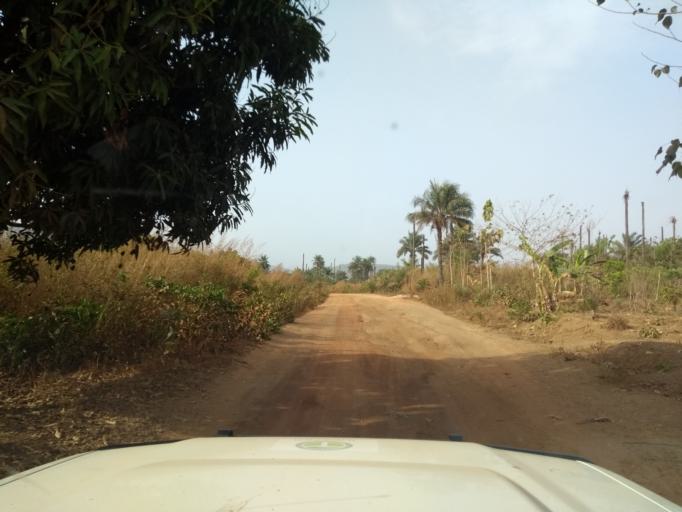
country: GN
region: Kindia
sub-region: Prefecture de Dubreka
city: Dubreka
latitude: 9.8802
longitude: -13.5387
